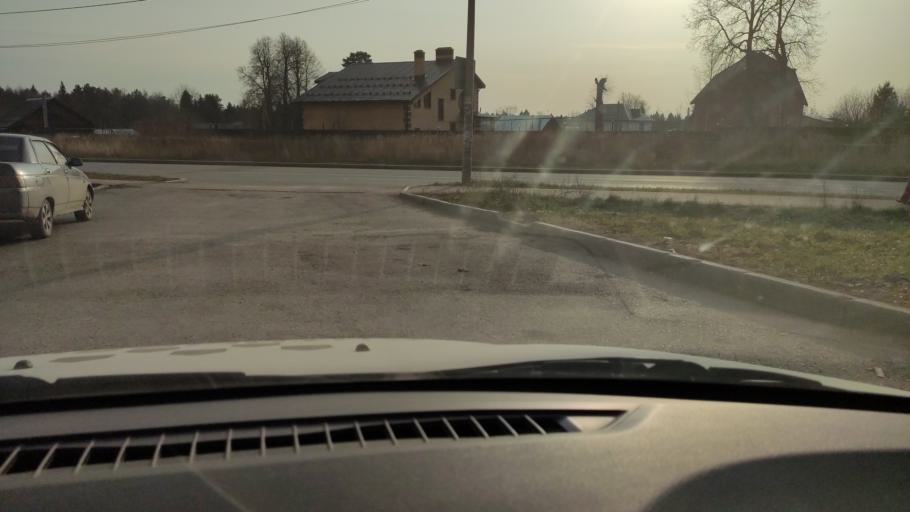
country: RU
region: Perm
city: Perm
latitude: 58.0851
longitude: 56.4004
